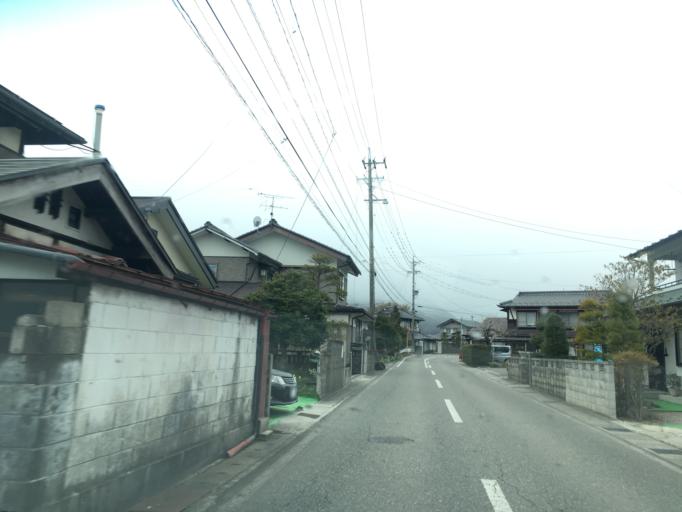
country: JP
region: Nagano
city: Omachi
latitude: 36.5103
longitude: 137.8504
